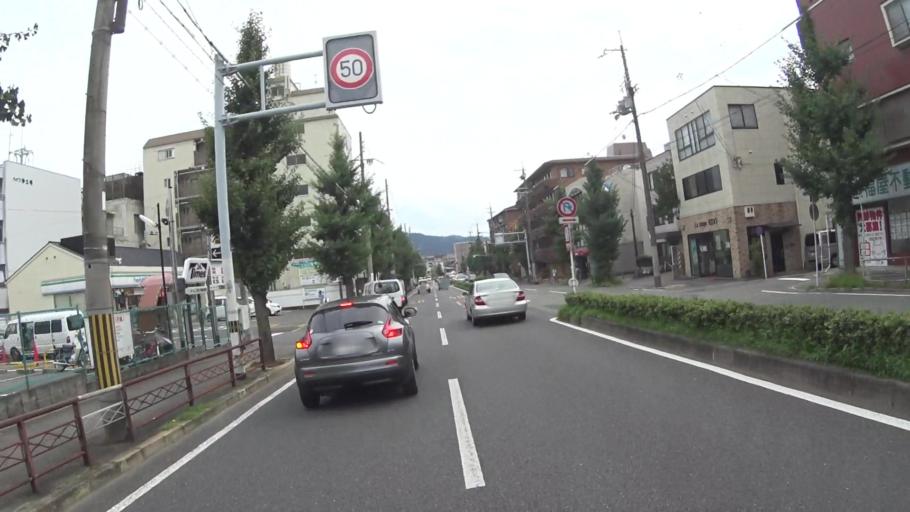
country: JP
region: Kyoto
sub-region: Kyoto-shi
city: Kamigyo-ku
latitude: 35.0244
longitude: 135.7920
